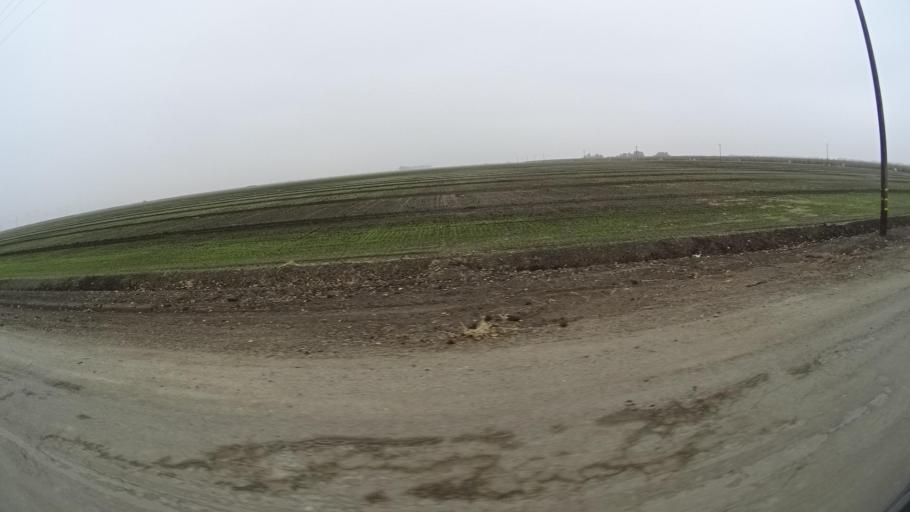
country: US
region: California
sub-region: Kern County
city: Lost Hills
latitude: 35.5867
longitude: -119.6110
